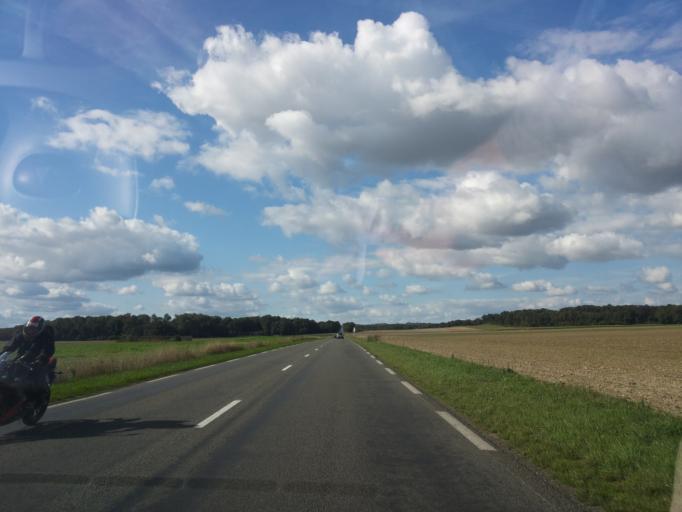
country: FR
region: Picardie
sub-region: Departement de l'Aisne
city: Saint-Erme-Outre-et-Ramecourt
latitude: 49.4458
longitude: 3.8452
